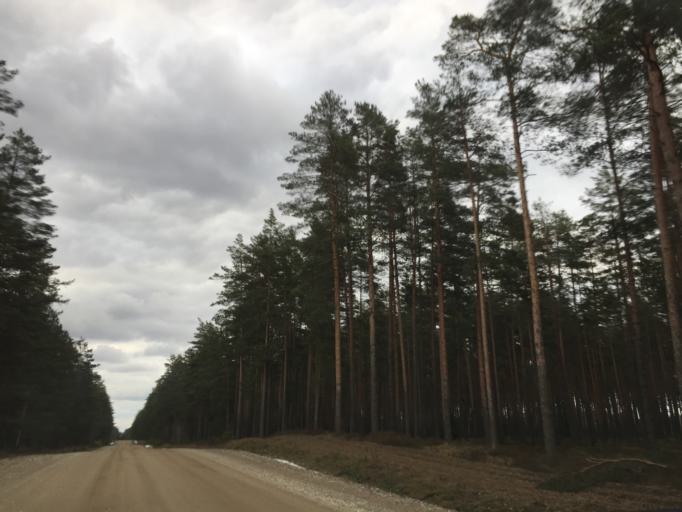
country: LV
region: Jaunjelgava
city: Jaunjelgava
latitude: 56.5805
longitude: 25.0255
